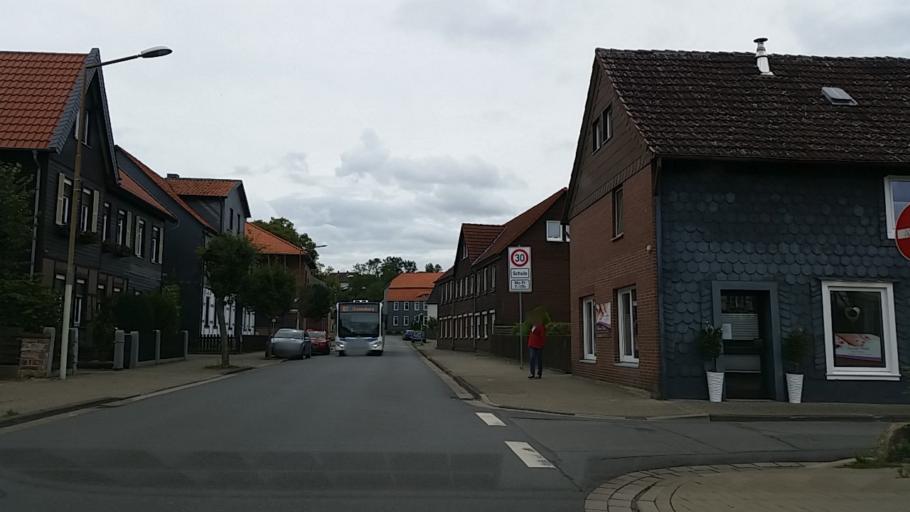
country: DE
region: Lower Saxony
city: Vienenburg
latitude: 51.9521
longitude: 10.5639
